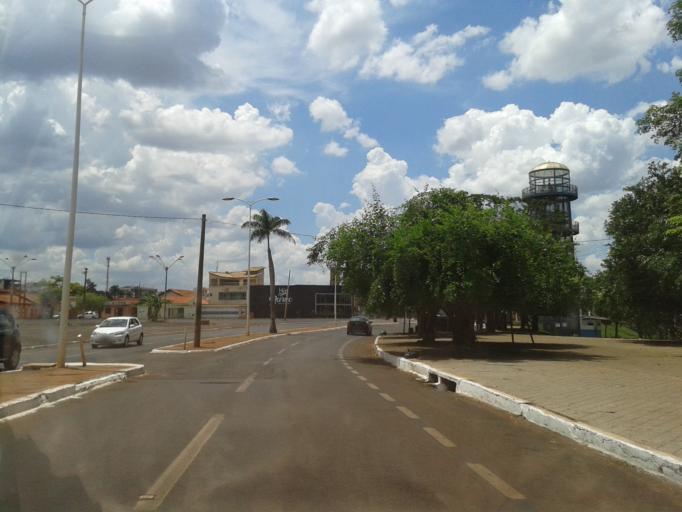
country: BR
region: Goias
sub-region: Itumbiara
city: Itumbiara
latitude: -18.4165
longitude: -49.2132
